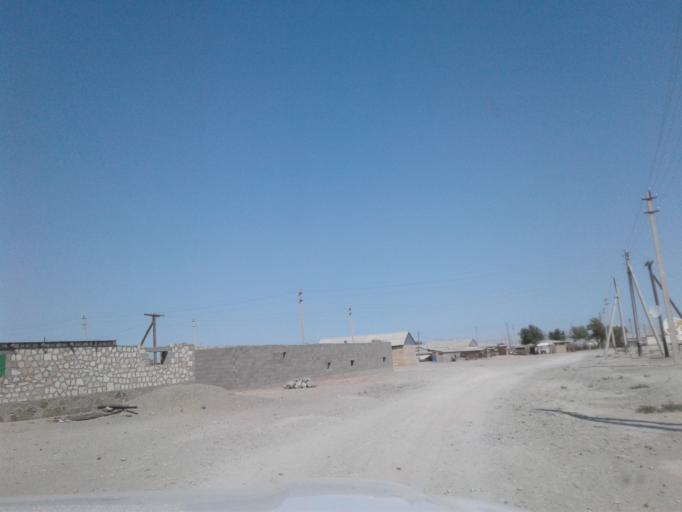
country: TM
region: Balkan
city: Gazanjyk
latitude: 39.1505
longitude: 55.3154
